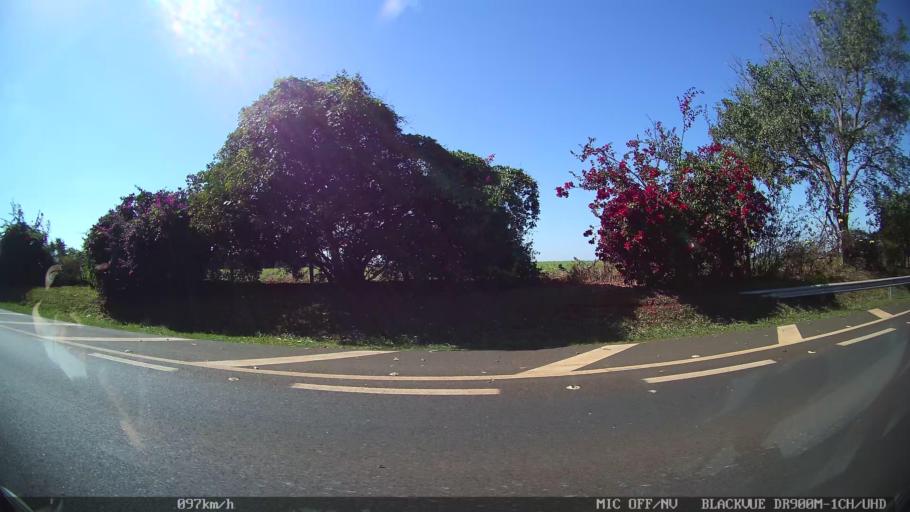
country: BR
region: Sao Paulo
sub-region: Batatais
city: Batatais
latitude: -20.7486
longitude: -47.5313
